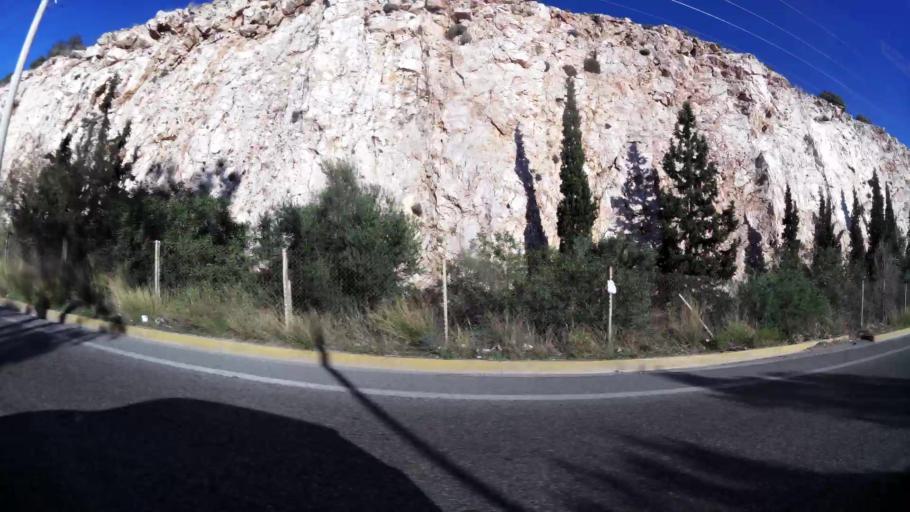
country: GR
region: Attica
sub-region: Nomarchia Athinas
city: Skaramangas
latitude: 37.9869
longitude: 23.5905
